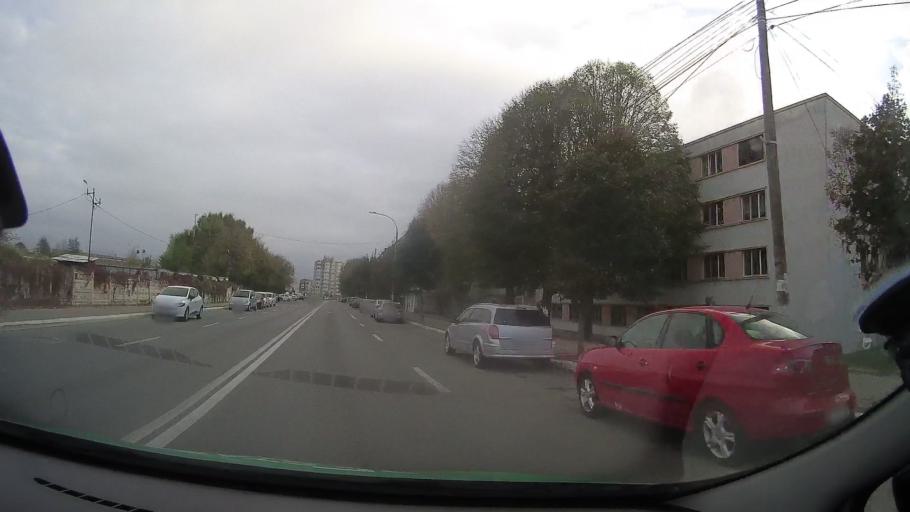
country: RO
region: Constanta
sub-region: Municipiul Medgidia
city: Medgidia
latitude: 44.2641
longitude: 28.2601
